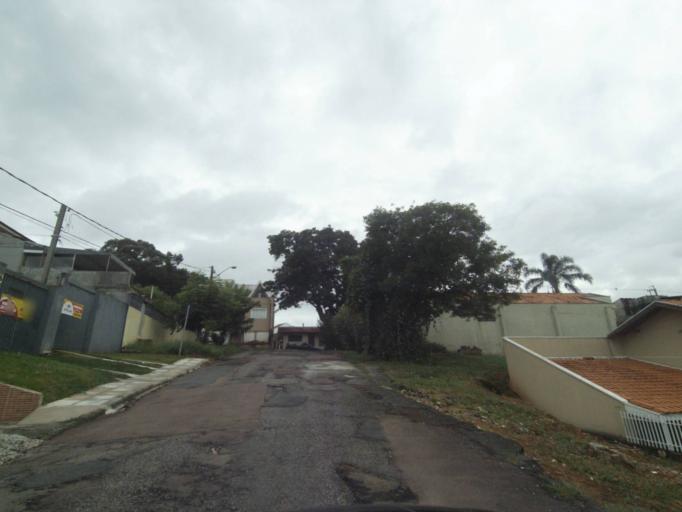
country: BR
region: Parana
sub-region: Curitiba
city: Curitiba
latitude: -25.4742
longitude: -49.3324
